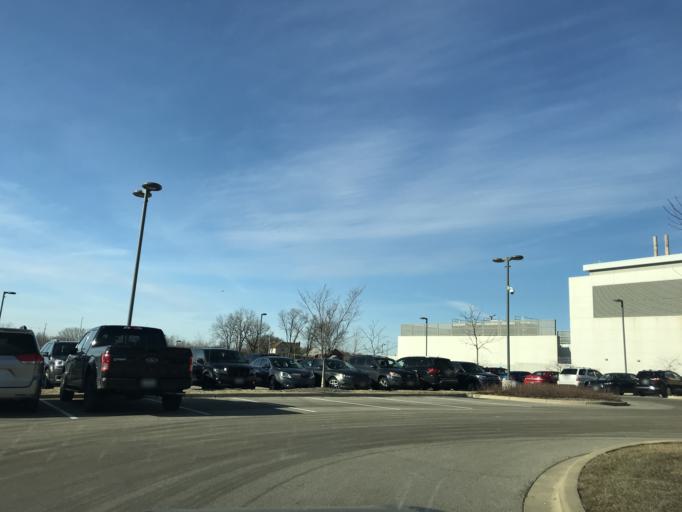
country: US
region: Wisconsin
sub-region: Dane County
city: Windsor
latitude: 43.1546
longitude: -89.3030
